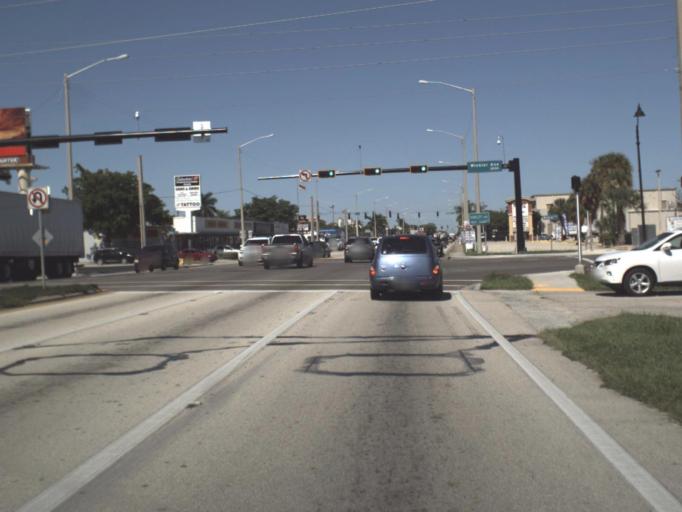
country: US
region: Florida
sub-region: Lee County
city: Pine Manor
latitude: 26.6038
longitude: -81.8718
